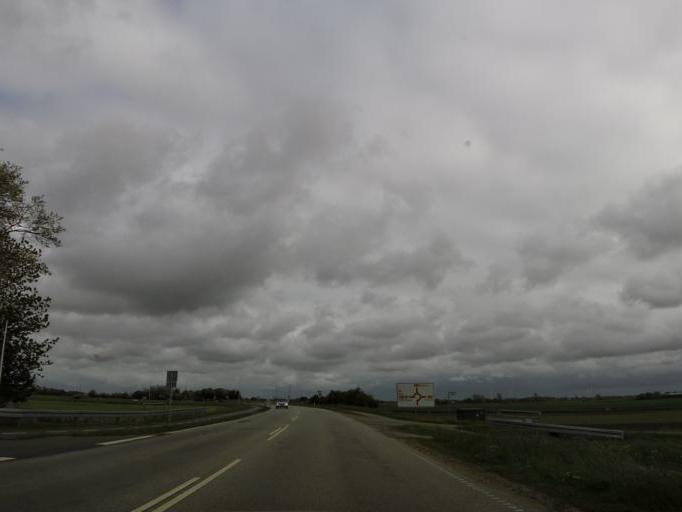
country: DK
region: South Denmark
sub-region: Tonder Kommune
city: Tonder
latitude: 54.9310
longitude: 8.8877
